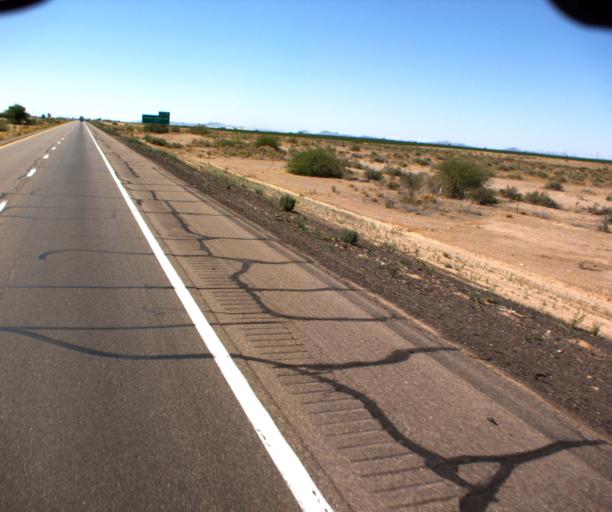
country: US
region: Arizona
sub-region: Maricopa County
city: Gila Bend
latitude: 32.9357
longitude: -112.7801
